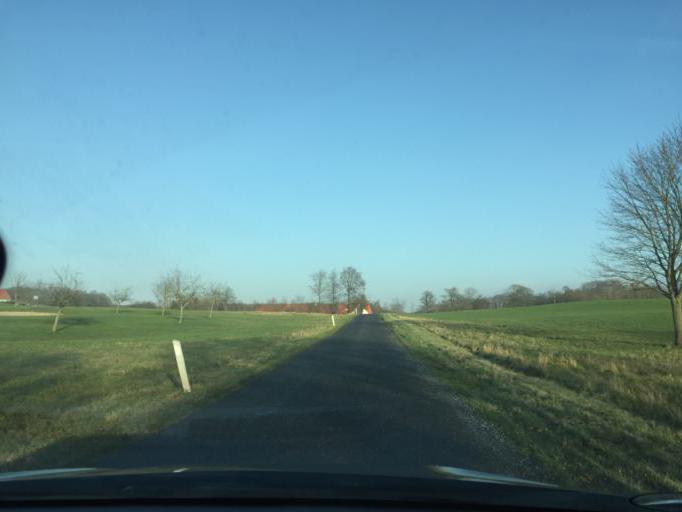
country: DK
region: South Denmark
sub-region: Faaborg-Midtfyn Kommune
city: Faaborg
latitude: 55.1354
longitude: 10.2486
